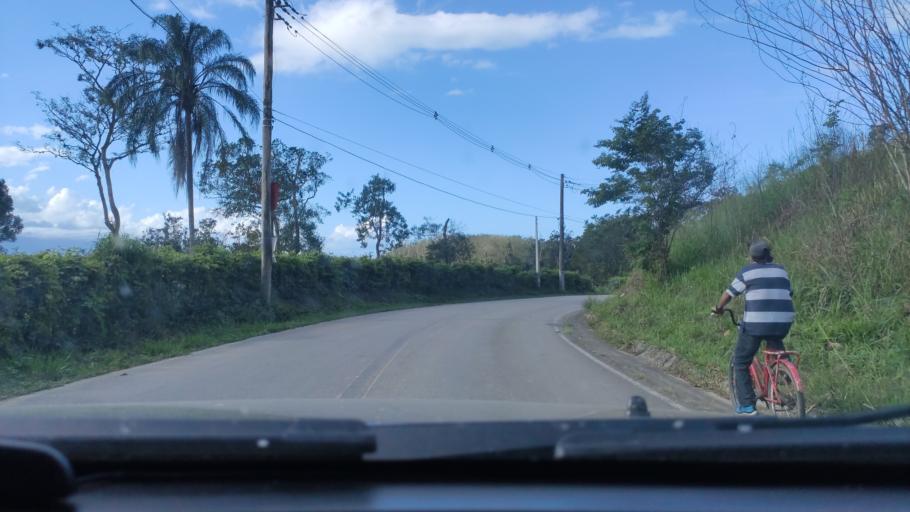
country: BR
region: Sao Paulo
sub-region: Sao Sebastiao
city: Sao Sebastiao
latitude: -23.6984
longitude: -45.4705
